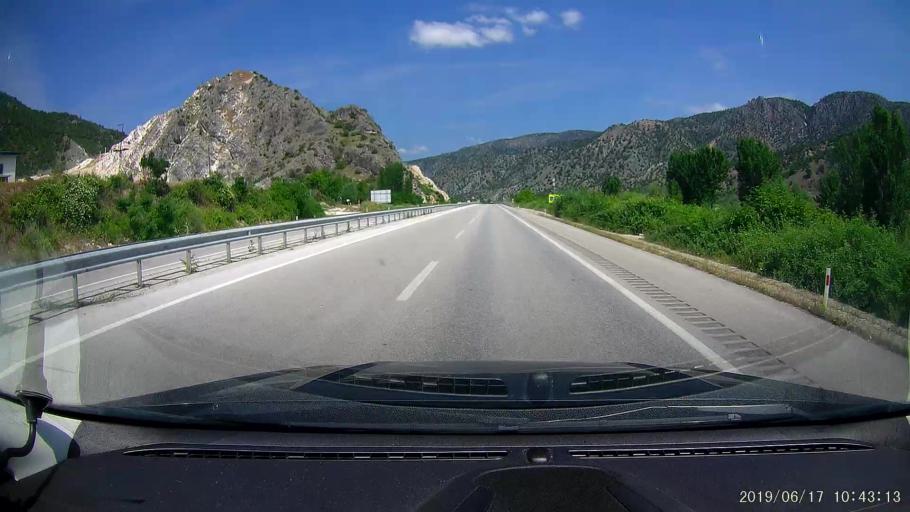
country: TR
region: Corum
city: Kargi
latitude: 41.0605
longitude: 34.5396
